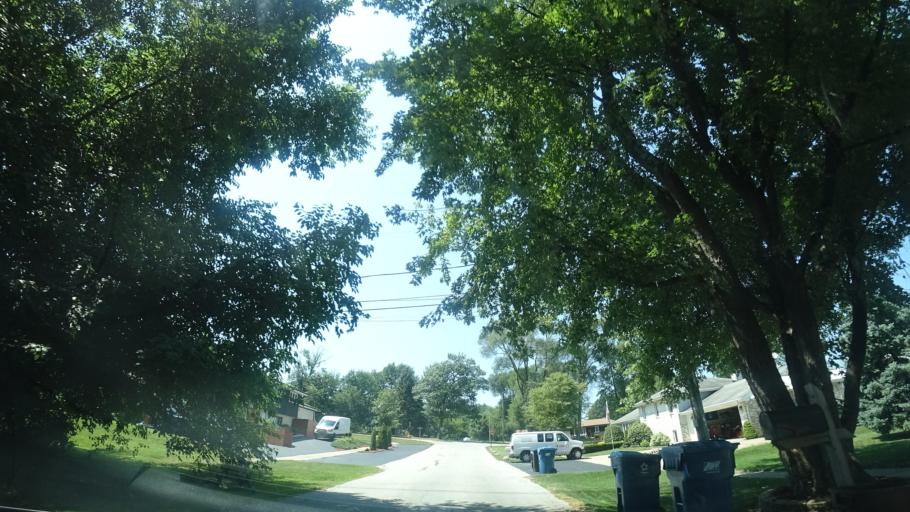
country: US
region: Illinois
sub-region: Cook County
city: Alsip
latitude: 41.6816
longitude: -87.7447
